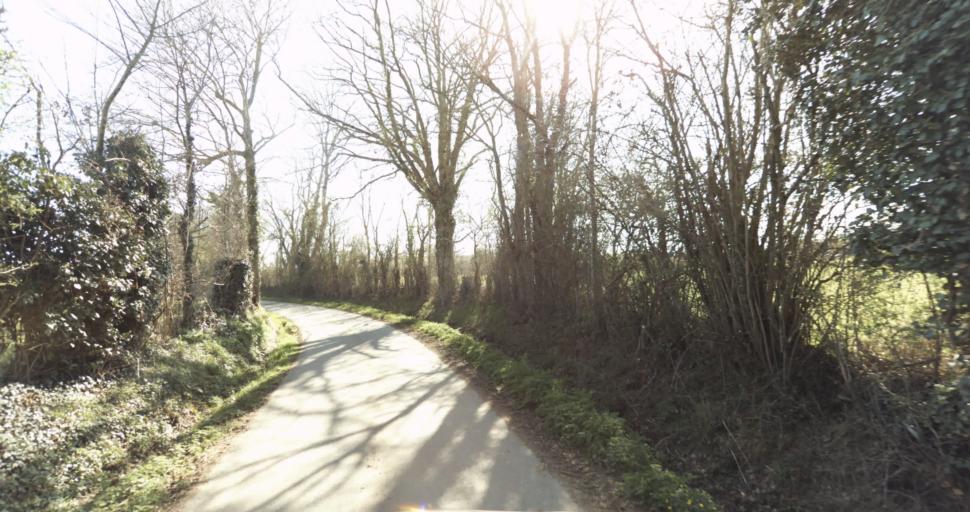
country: FR
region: Lower Normandy
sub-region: Departement du Calvados
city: Saint-Pierre-sur-Dives
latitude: 49.0500
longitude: 0.0546
